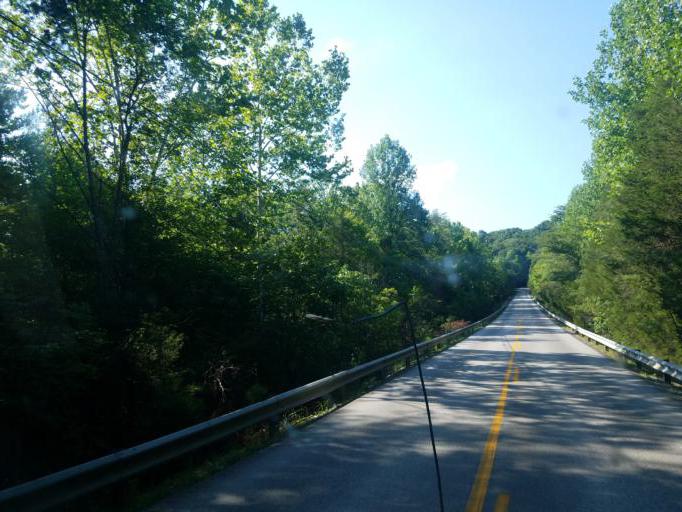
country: US
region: Kentucky
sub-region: Hart County
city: Munfordville
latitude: 37.3329
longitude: -86.0563
